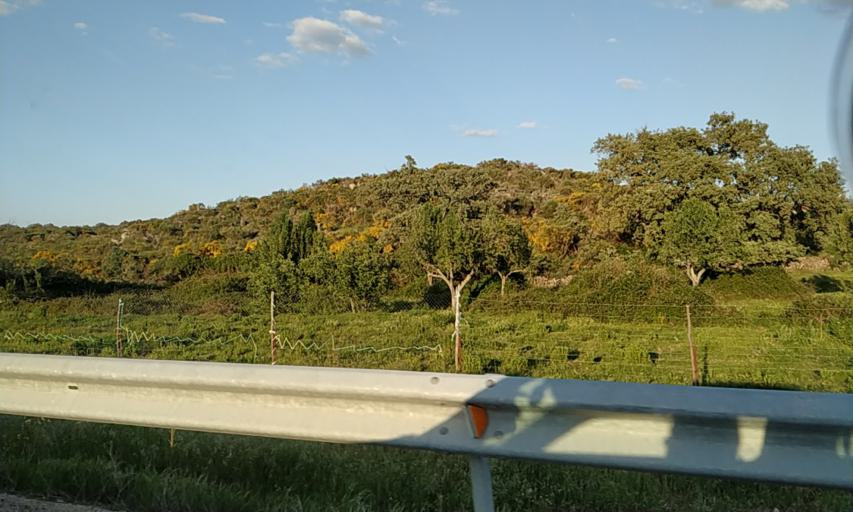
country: PT
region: Portalegre
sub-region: Portalegre
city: Sao Juliao
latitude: 39.3531
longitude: -7.2743
